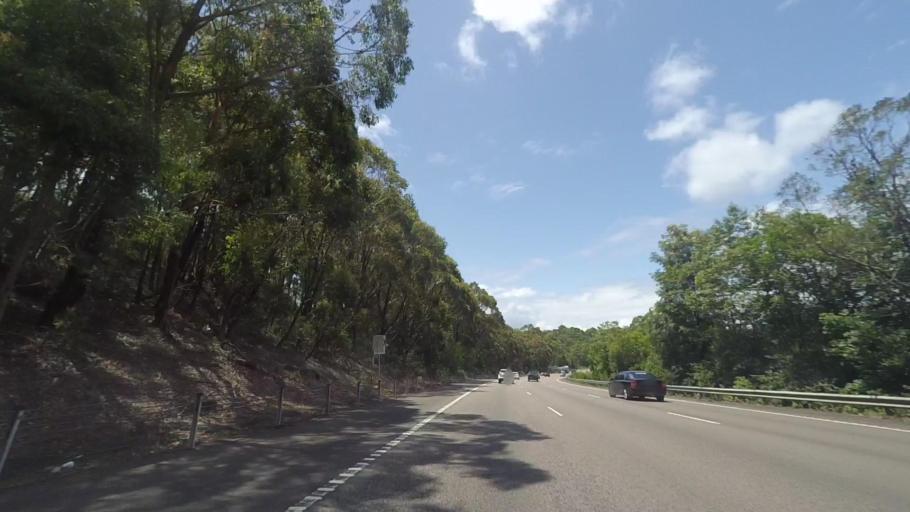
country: AU
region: New South Wales
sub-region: Gosford Shire
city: Lisarow
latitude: -33.3629
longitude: 151.3336
